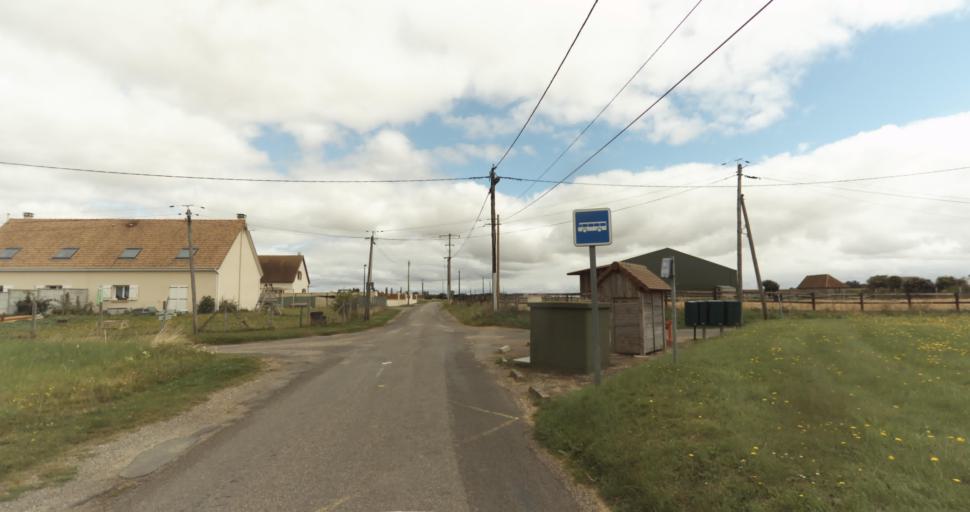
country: FR
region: Haute-Normandie
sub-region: Departement de l'Eure
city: Evreux
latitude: 48.9348
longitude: 1.2213
